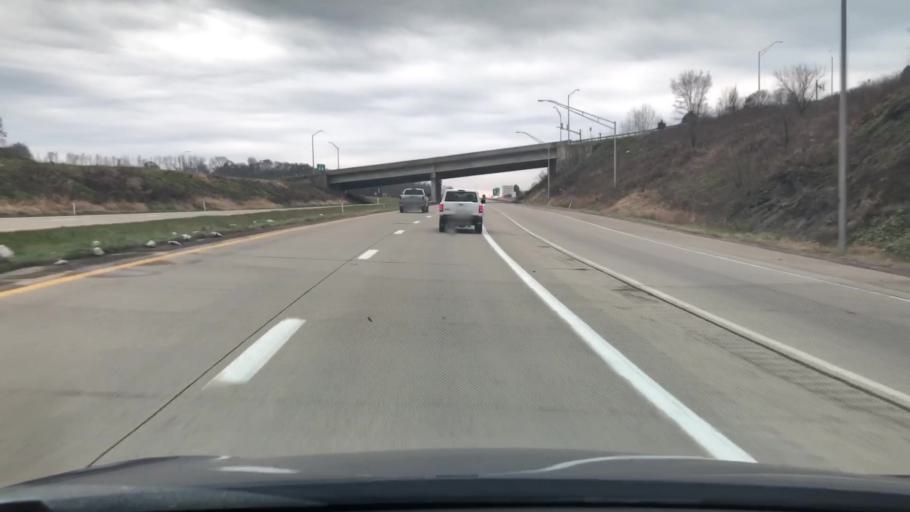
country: US
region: Pennsylvania
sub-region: Armstrong County
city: Kittanning
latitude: 40.8060
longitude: -79.4886
